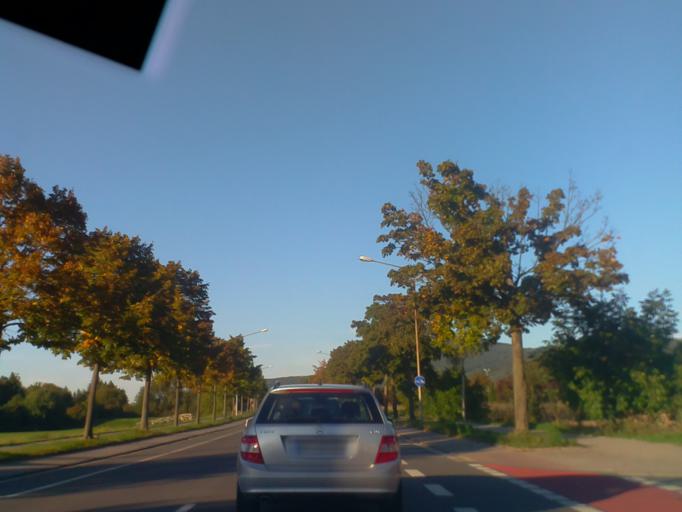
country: DE
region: Hesse
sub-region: Regierungsbezirk Darmstadt
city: Bensheim
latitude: 49.6912
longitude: 8.6091
